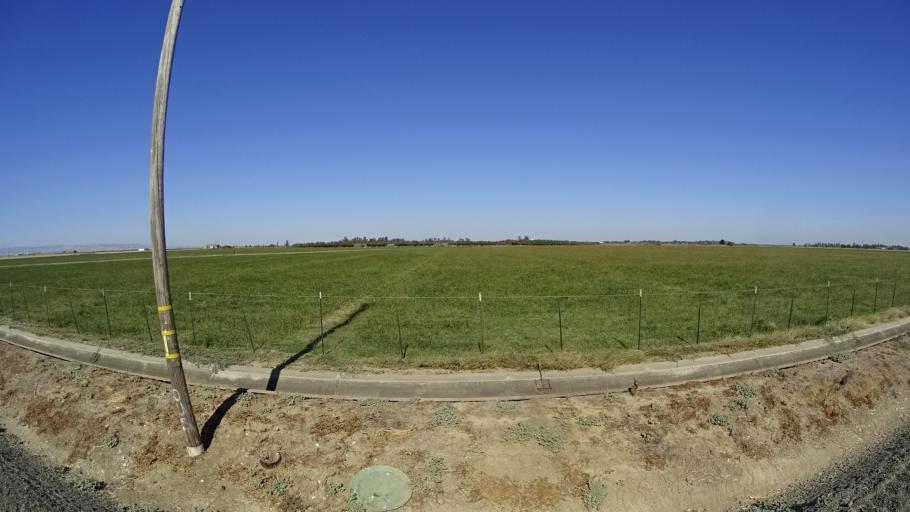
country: US
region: California
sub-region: Yolo County
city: Cottonwood
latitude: 38.6200
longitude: -121.8915
